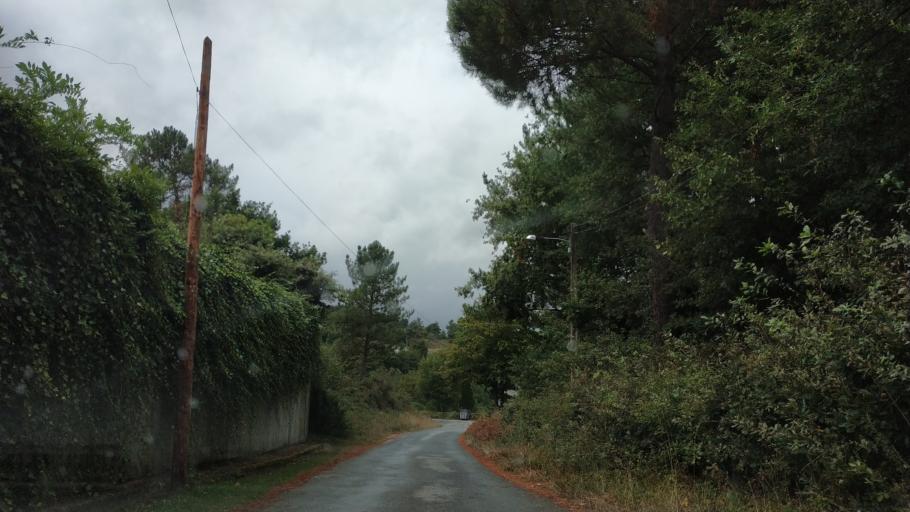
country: ES
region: Galicia
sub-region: Provincia de Lugo
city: Lugo
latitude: 42.9951
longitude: -7.5728
